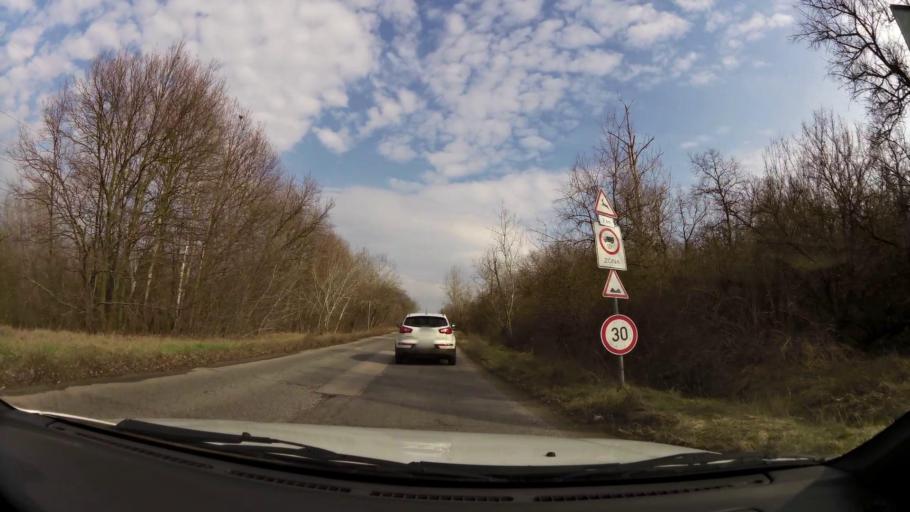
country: HU
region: Budapest
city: Budapest XVII. keruelet
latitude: 47.5102
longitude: 19.2358
